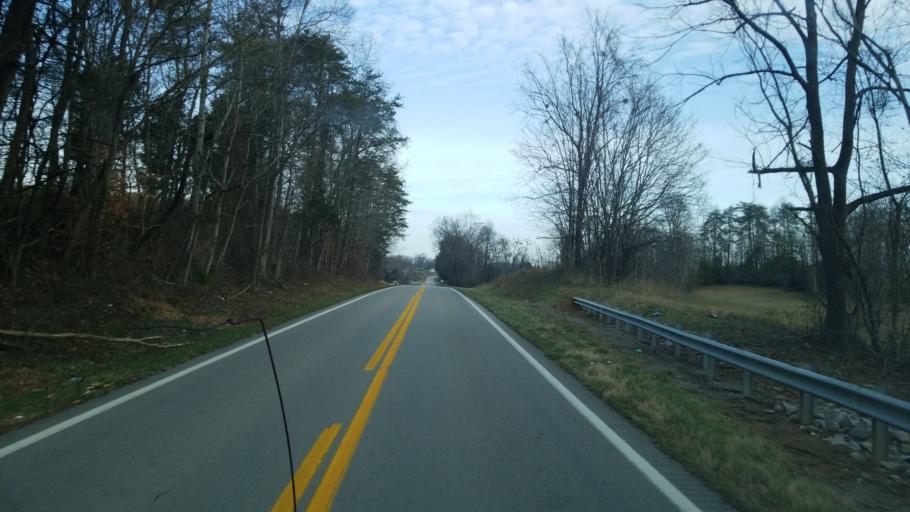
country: US
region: Kentucky
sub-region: Clinton County
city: Albany
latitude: 36.7977
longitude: -85.1810
